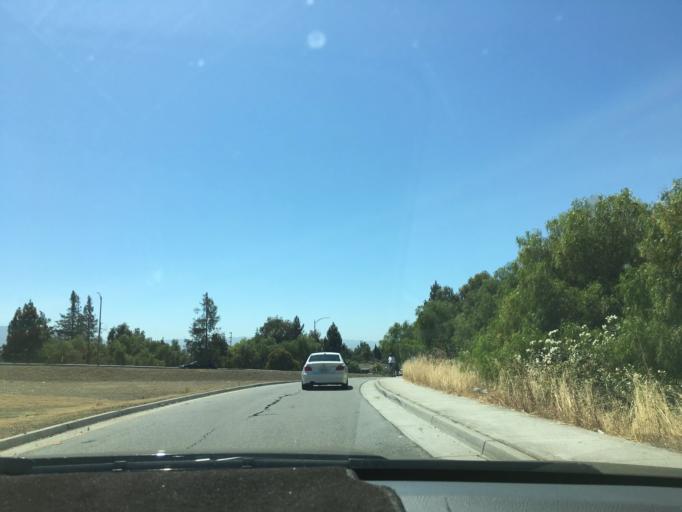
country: US
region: California
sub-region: Santa Clara County
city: Seven Trees
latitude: 37.2572
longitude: -121.8007
